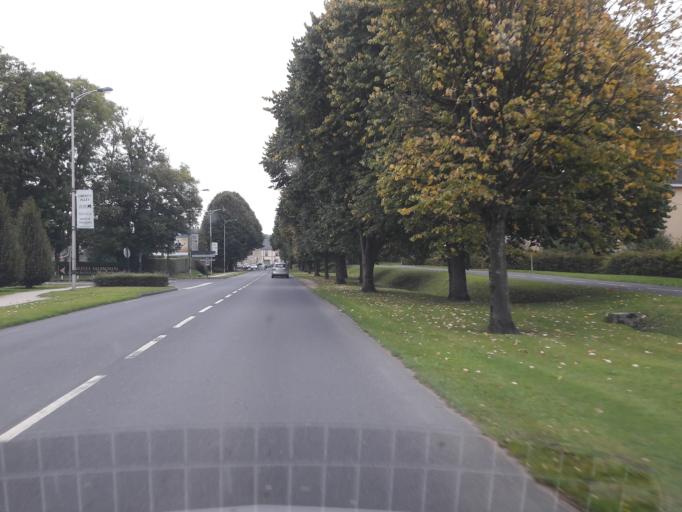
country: FR
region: Lower Normandy
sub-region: Departement du Calvados
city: Bayeux
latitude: 49.2727
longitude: -0.7116
